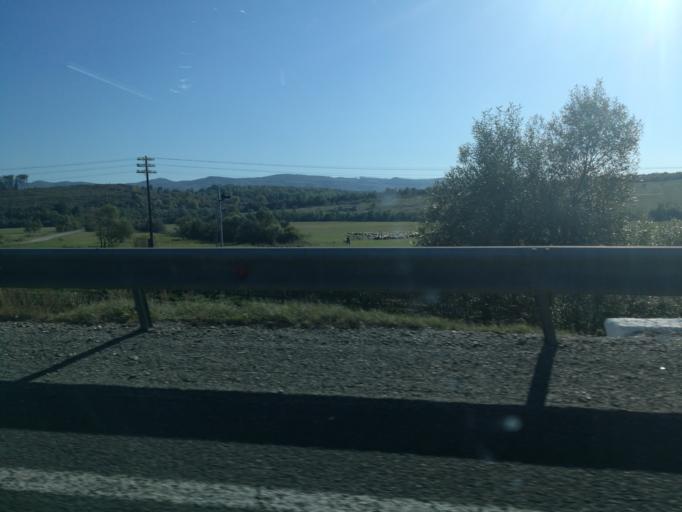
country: RO
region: Brasov
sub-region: Comuna Dumbravita
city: Dumbravita
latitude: 45.7715
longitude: 25.3546
